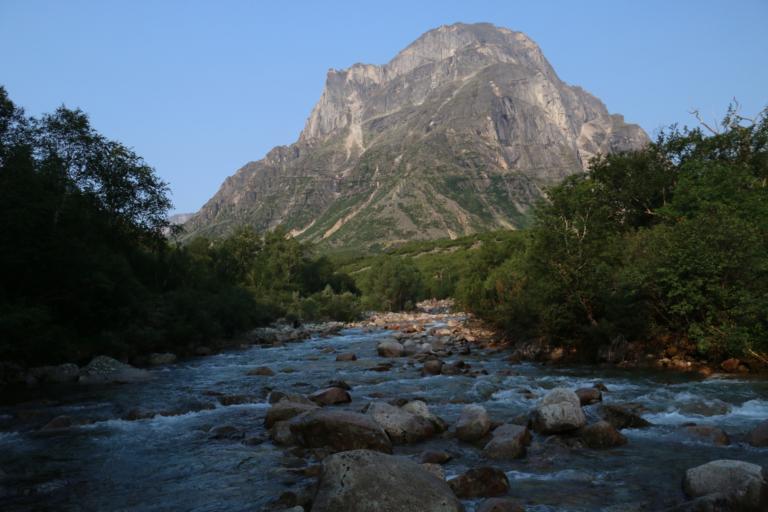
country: RU
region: Respublika Buryatiya
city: Novyy Uoyan
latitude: 56.2714
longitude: 111.1042
